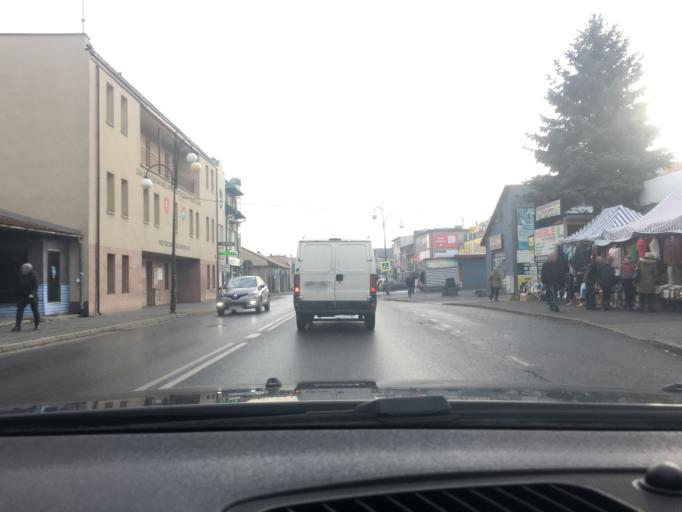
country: PL
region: Swietokrzyskie
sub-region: Powiat jedrzejowski
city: Jedrzejow
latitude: 50.6416
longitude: 20.3006
